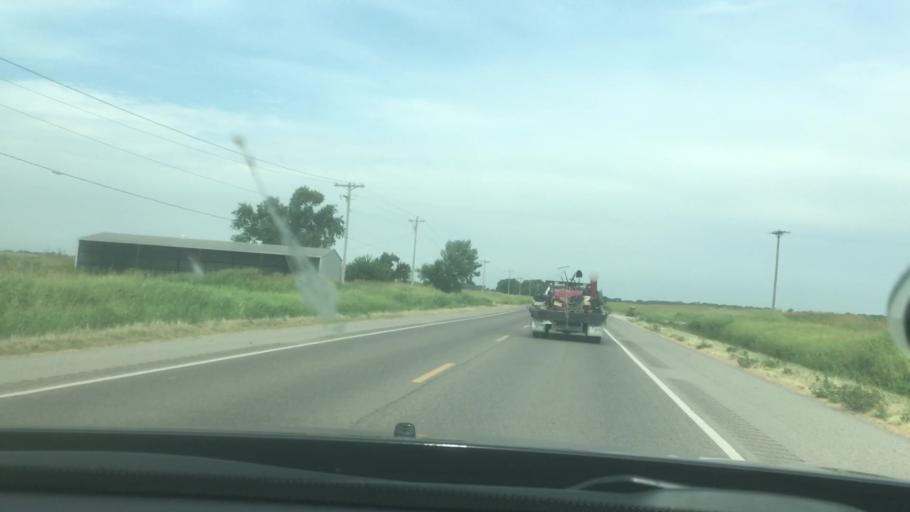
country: US
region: Oklahoma
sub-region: Garvin County
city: Lindsay
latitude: 34.8243
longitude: -97.5359
